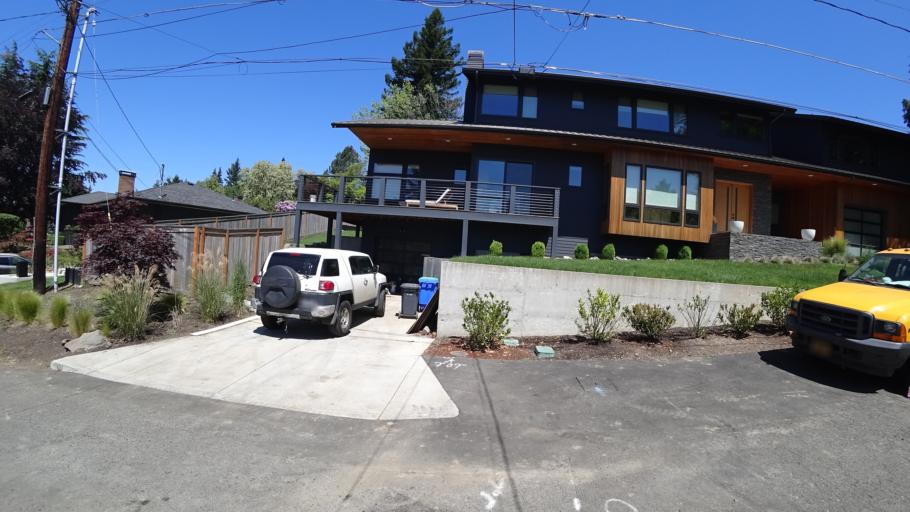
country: US
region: Oregon
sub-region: Multnomah County
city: Portland
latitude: 45.4900
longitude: -122.7096
